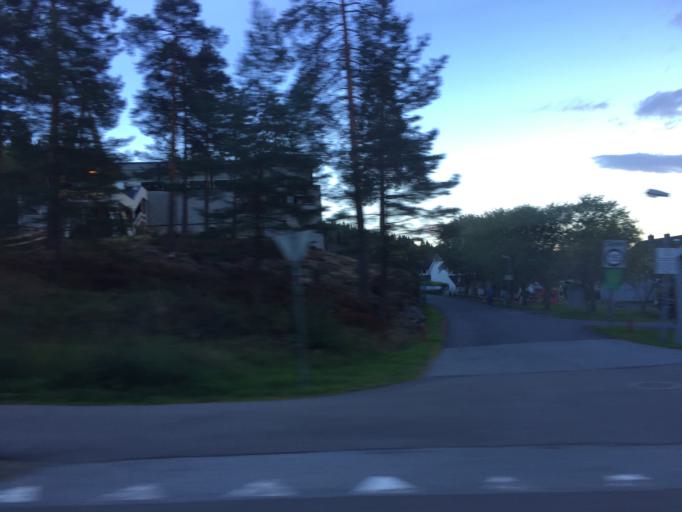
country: NO
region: Akershus
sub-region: Skedsmo
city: Lillestrom
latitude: 59.9331
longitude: 11.0260
